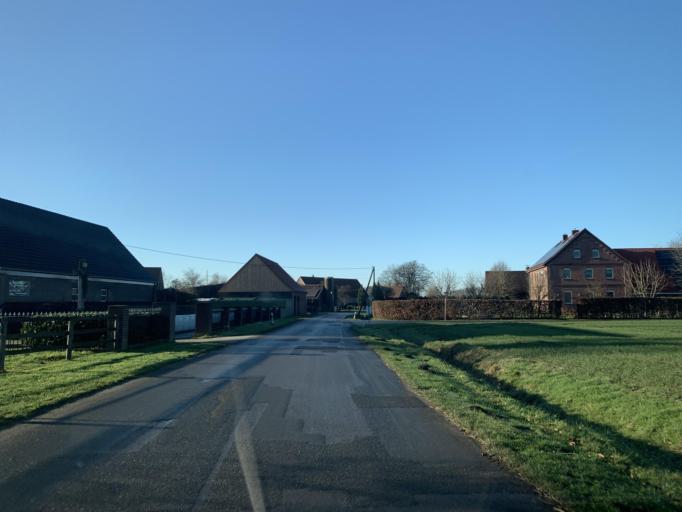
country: DE
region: North Rhine-Westphalia
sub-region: Regierungsbezirk Munster
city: Dulmen
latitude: 51.8777
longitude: 7.2845
